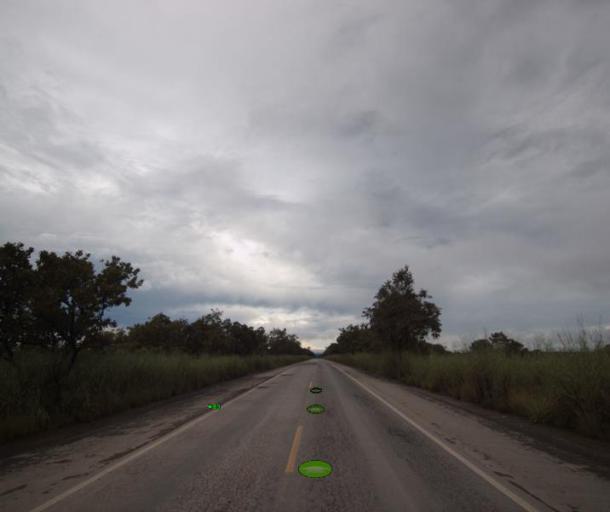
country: BR
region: Goias
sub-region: Porangatu
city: Porangatu
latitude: -13.5396
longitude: -49.1062
